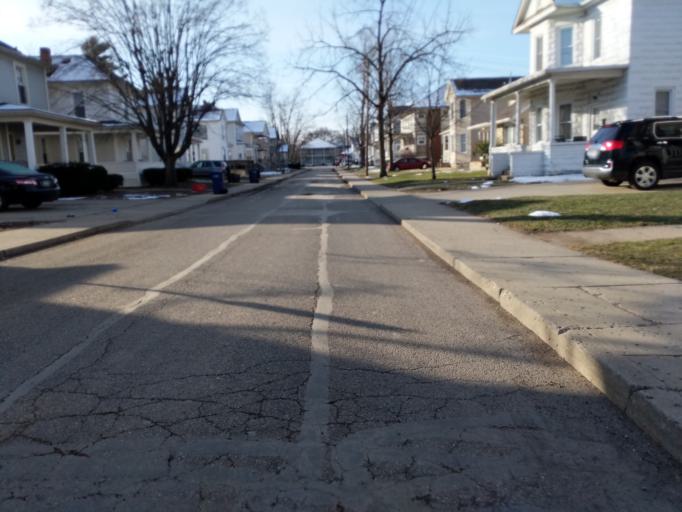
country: US
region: Ohio
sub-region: Athens County
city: Athens
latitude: 39.3311
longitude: -82.0955
